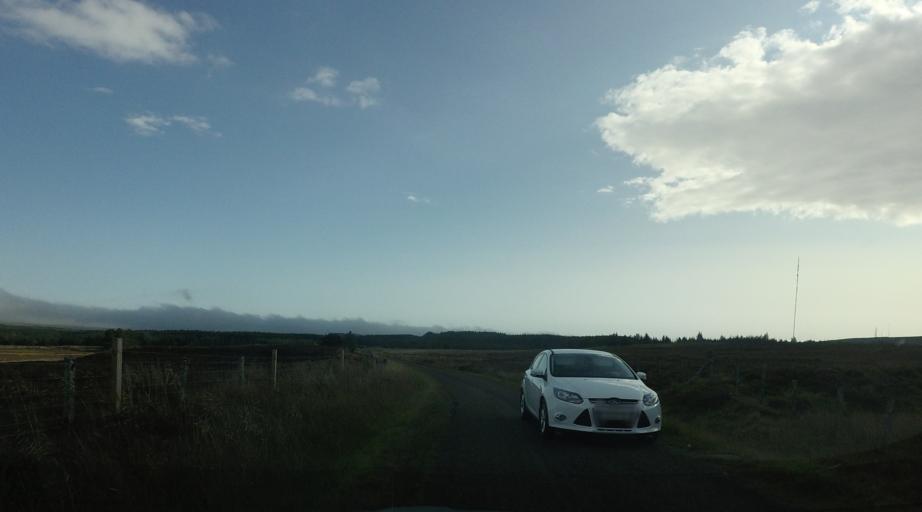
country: GB
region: Scotland
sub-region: Highland
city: Thurso
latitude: 58.3431
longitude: -3.3700
